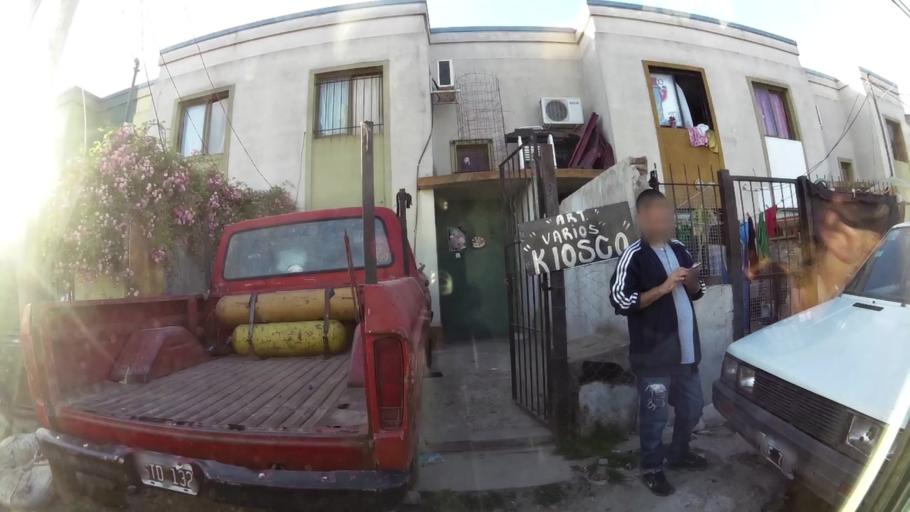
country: AR
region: Buenos Aires
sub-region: Partido de San Isidro
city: San Isidro
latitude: -34.4709
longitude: -58.5444
